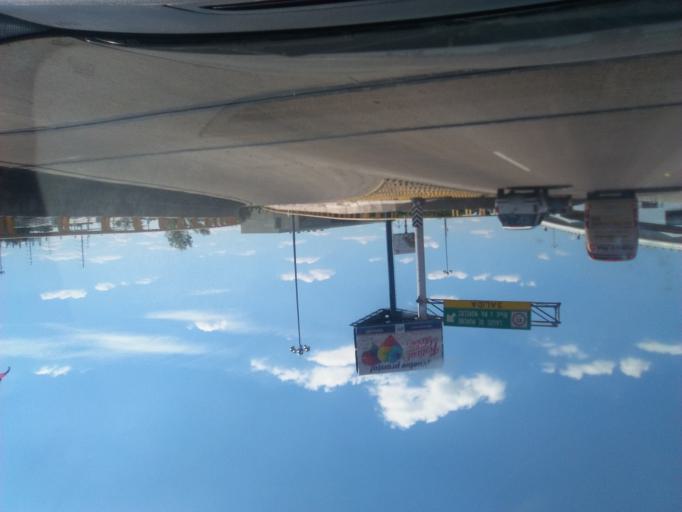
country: MX
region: Guanajuato
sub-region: Leon
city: Fraccionamiento Paraiso Real
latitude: 21.0964
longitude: -101.6283
